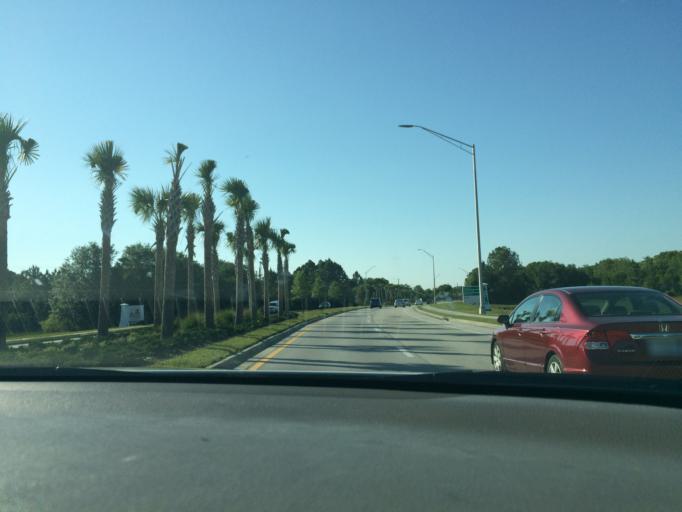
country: US
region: Florida
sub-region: Sarasota County
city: The Meadows
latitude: 27.4376
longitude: -82.4299
